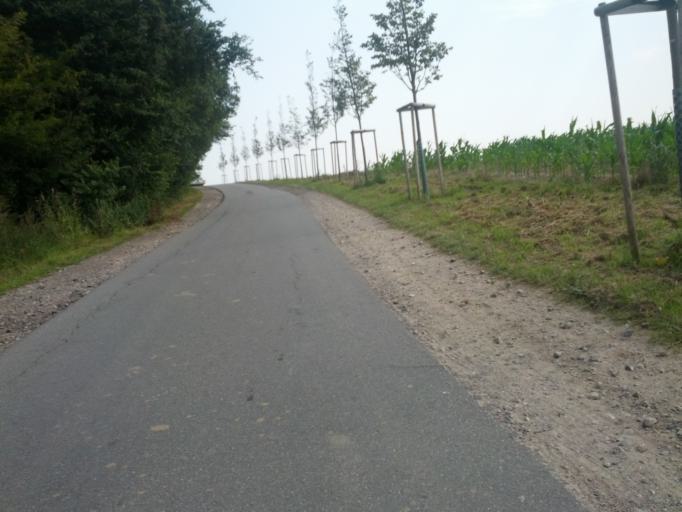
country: DE
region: Mecklenburg-Vorpommern
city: Bastorf
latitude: 54.1305
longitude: 11.6693
